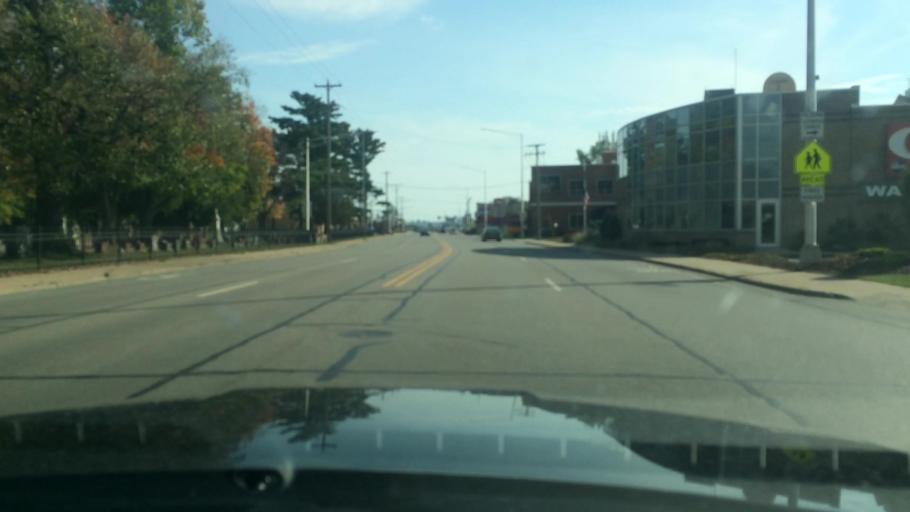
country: US
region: Wisconsin
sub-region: Marathon County
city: Wausau
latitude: 44.9380
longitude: -89.6180
